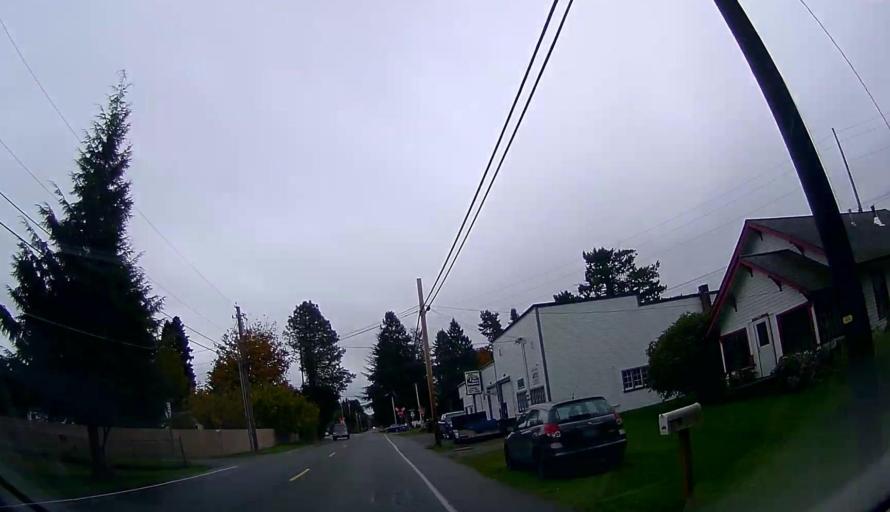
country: US
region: Washington
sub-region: Skagit County
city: Sedro-Woolley
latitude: 48.5032
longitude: -122.2141
